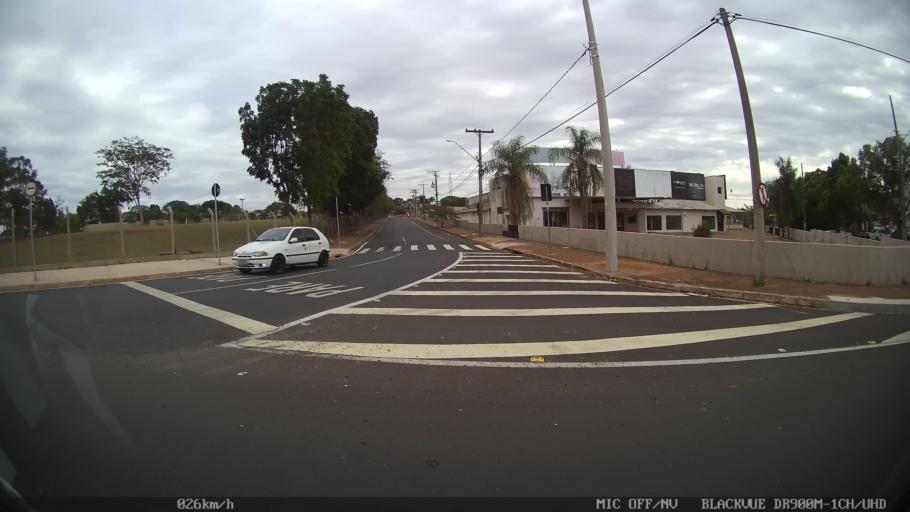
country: BR
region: Sao Paulo
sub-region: Sao Jose Do Rio Preto
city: Sao Jose do Rio Preto
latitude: -20.8222
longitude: -49.4181
